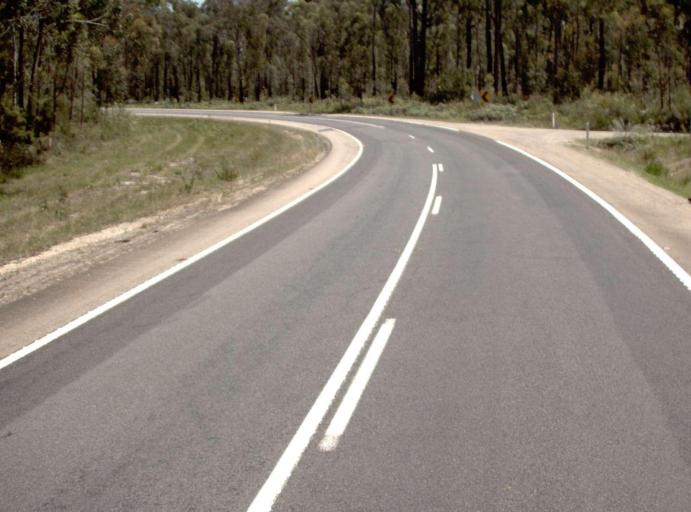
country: AU
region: Victoria
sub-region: East Gippsland
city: Lakes Entrance
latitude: -37.6876
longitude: 148.7520
